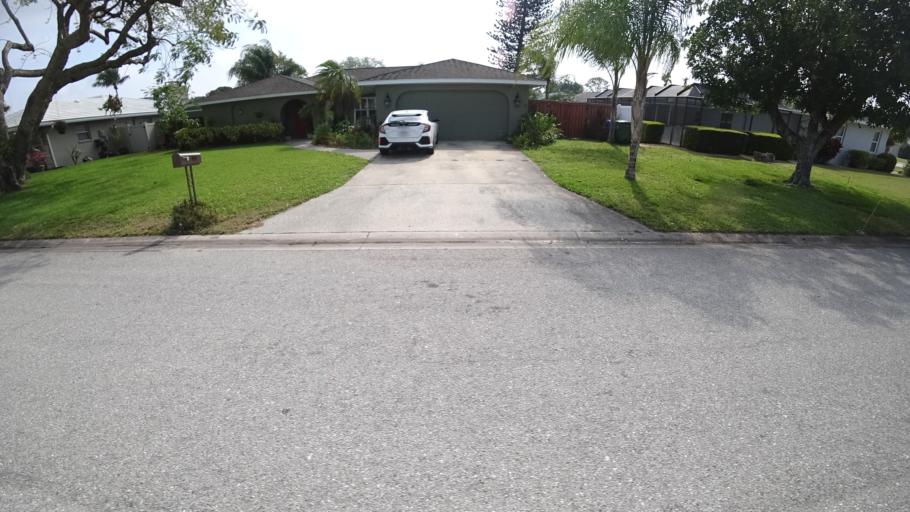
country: US
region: Florida
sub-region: Manatee County
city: West Bradenton
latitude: 27.4853
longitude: -82.6159
